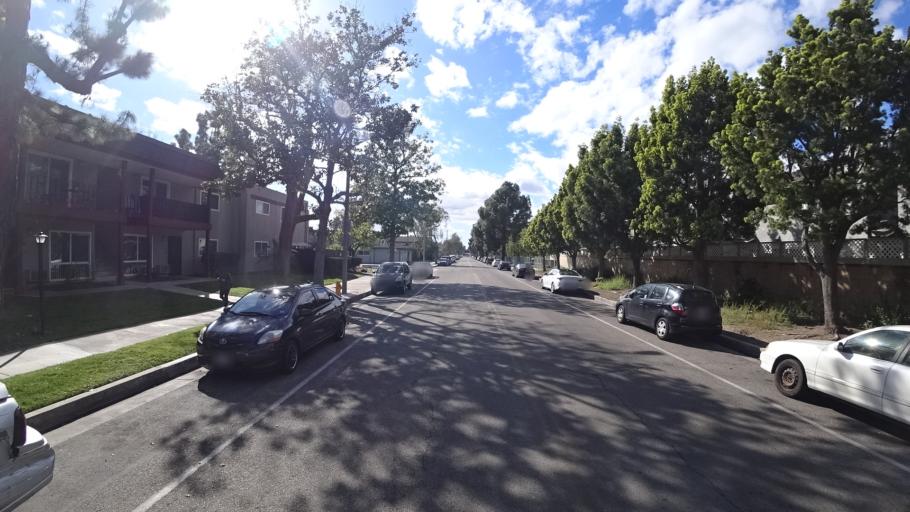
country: US
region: California
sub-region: Orange County
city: Anaheim
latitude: 33.8379
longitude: -117.9542
